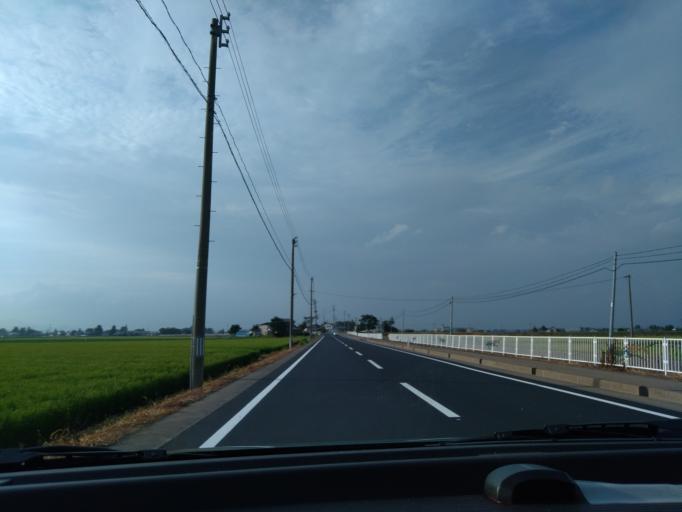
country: JP
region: Akita
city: Yokotemachi
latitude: 39.3757
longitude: 140.5343
